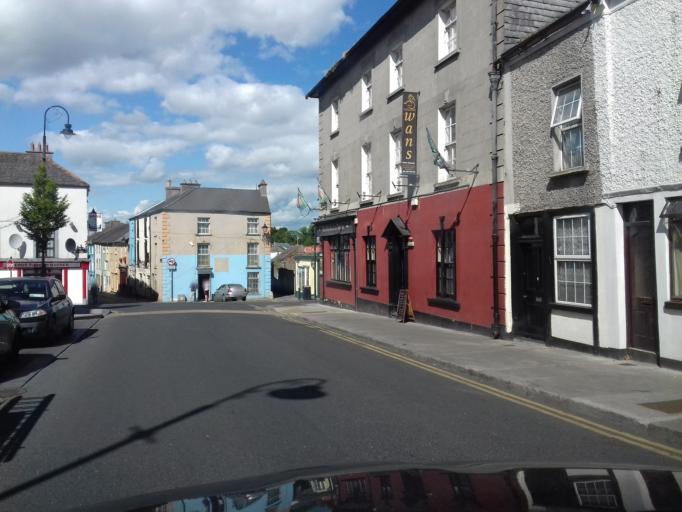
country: IE
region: Leinster
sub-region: Kilkenny
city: Callan
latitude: 52.5442
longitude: -7.3904
